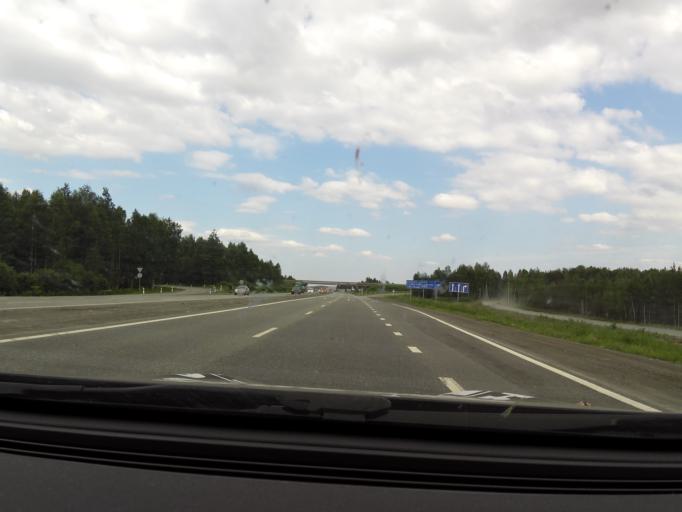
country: RU
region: Sverdlovsk
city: Talitsa
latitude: 56.8377
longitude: 60.1428
